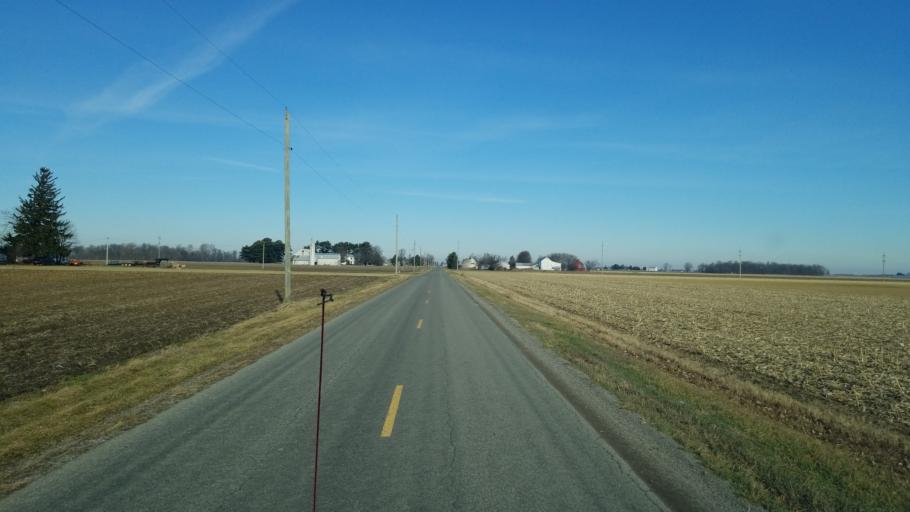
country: US
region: Ohio
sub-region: Putnam County
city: Pandora
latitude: 40.9376
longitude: -83.9378
